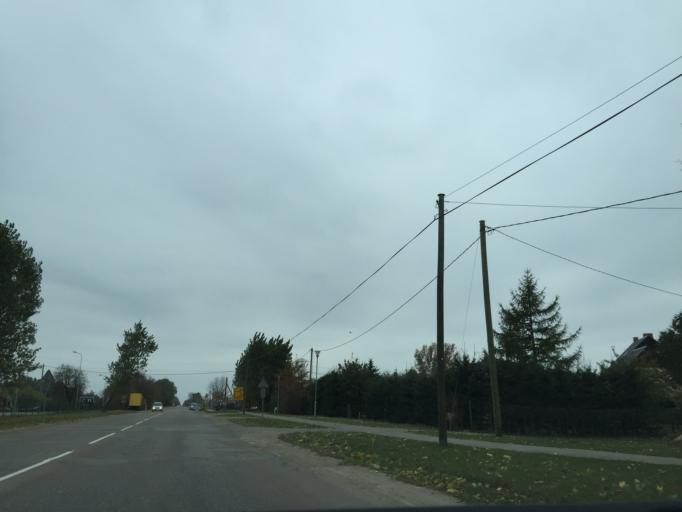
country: LV
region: Marupe
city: Marupe
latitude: 56.8922
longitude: 24.0736
